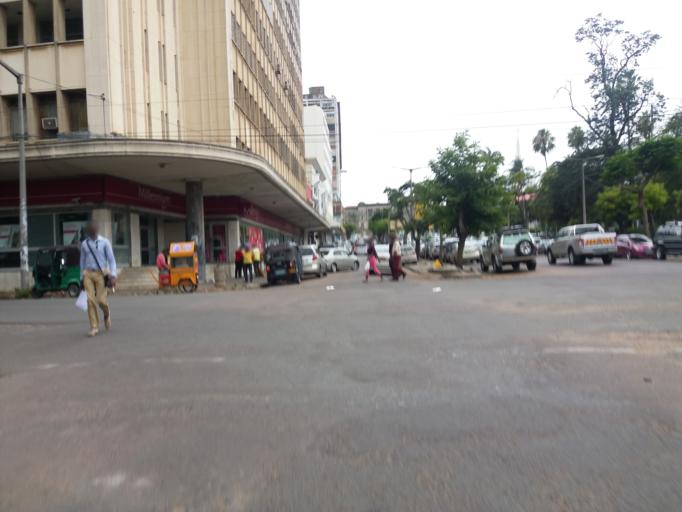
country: MZ
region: Maputo City
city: Maputo
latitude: -25.9718
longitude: 32.5715
